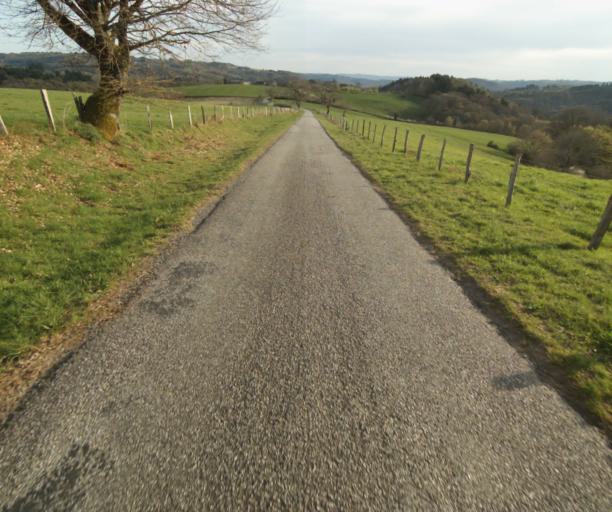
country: FR
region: Limousin
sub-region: Departement de la Correze
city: Correze
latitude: 45.3699
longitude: 1.8330
